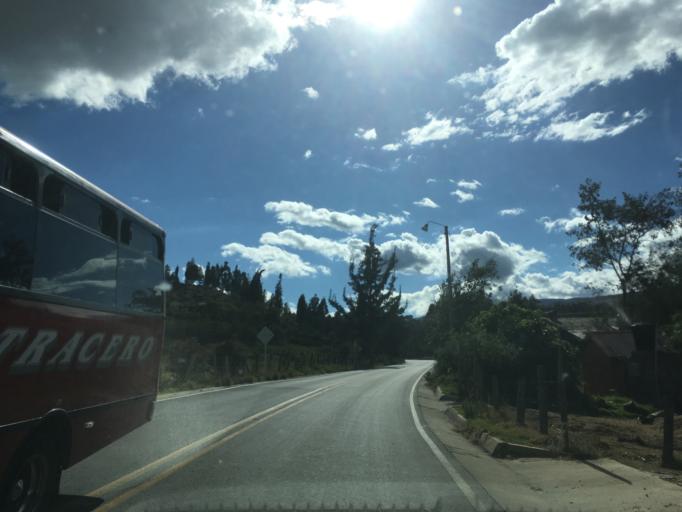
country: CO
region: Boyaca
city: Firavitoba
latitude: 5.6159
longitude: -73.0146
